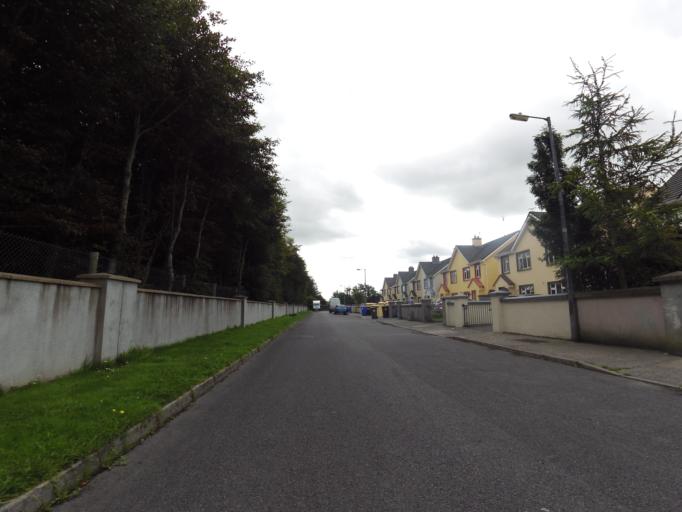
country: IE
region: Connaught
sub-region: County Galway
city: Athenry
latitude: 53.3036
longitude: -8.7398
